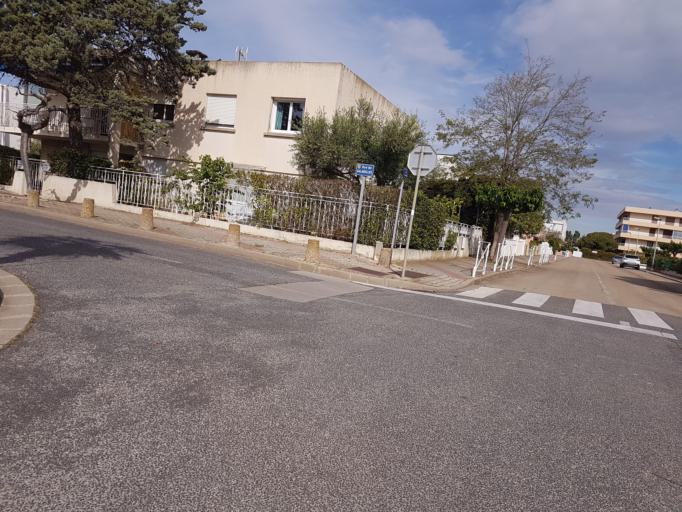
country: FR
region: Languedoc-Roussillon
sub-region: Departement du Gard
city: Le Grau-du-Roi
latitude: 43.5447
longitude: 4.1290
